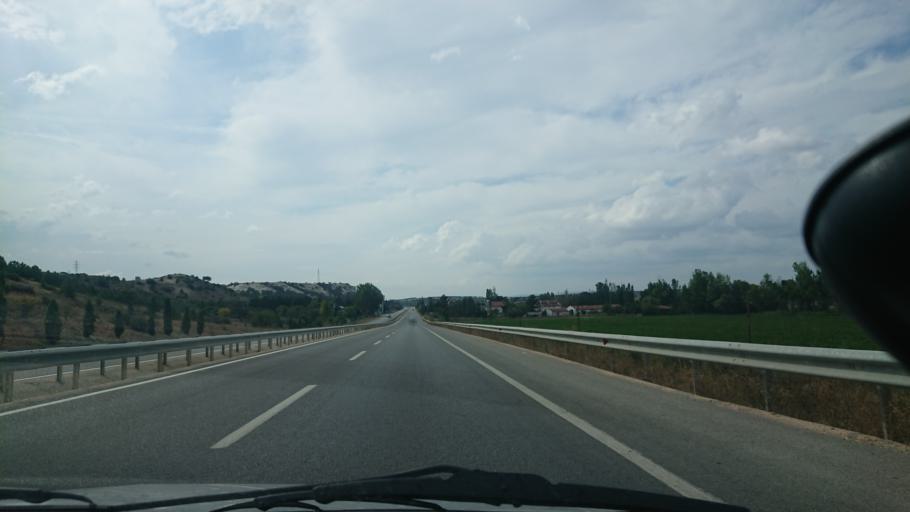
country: TR
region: Eskisehir
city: Eskisehir
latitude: 39.7267
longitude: 30.3687
